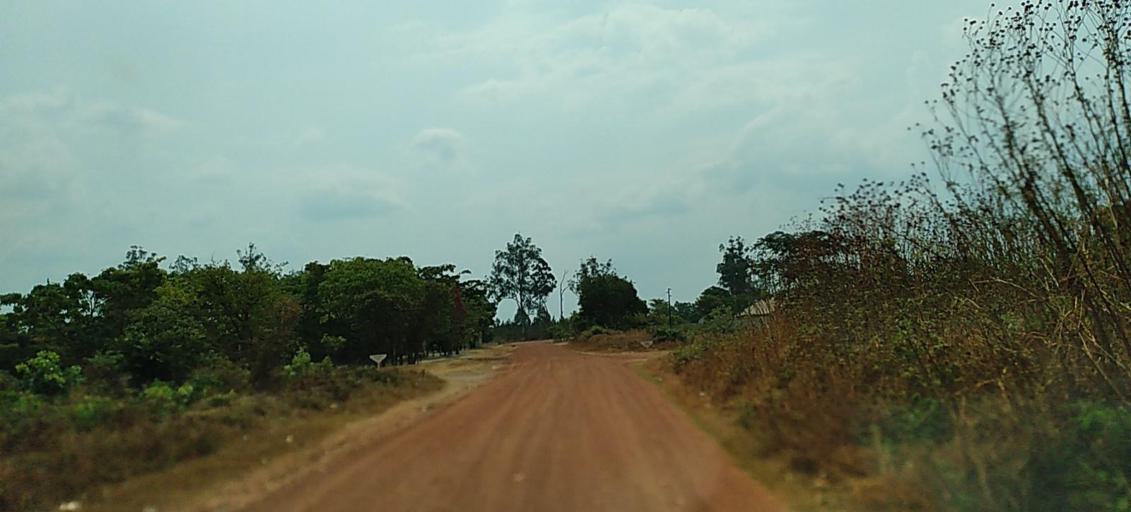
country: ZM
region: Copperbelt
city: Kalulushi
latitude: -12.8325
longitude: 28.0797
